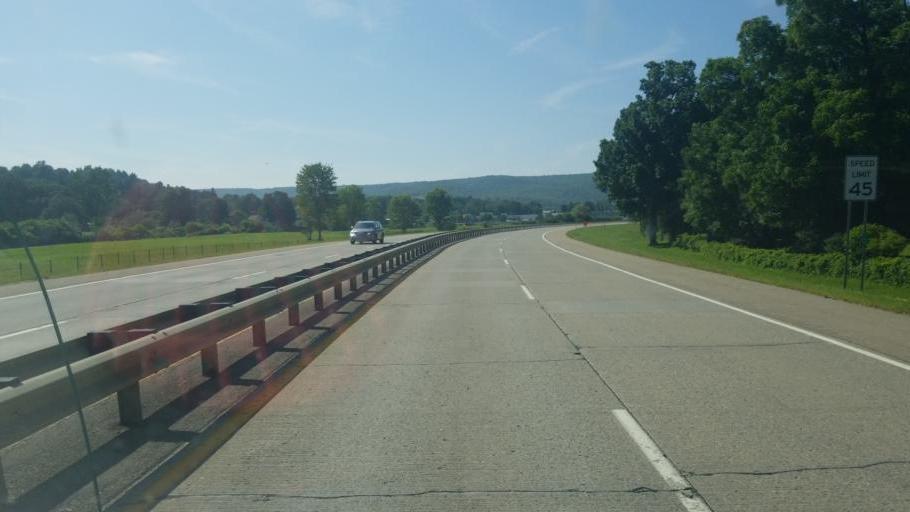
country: US
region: New York
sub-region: Allegany County
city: Wellsville
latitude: 42.1227
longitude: -77.9542
